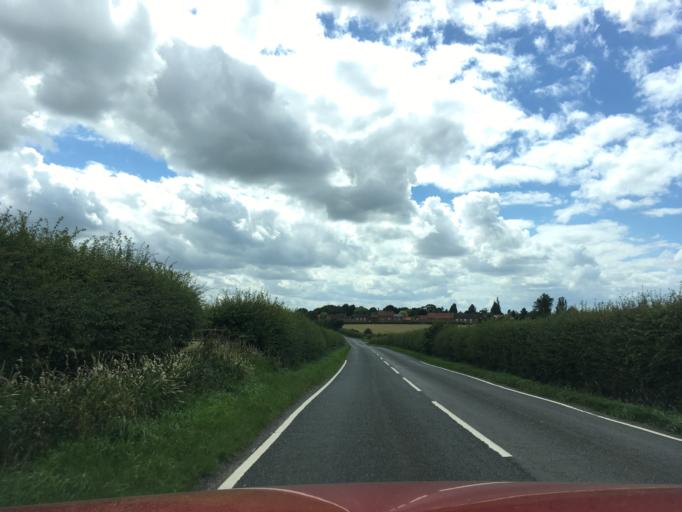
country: GB
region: England
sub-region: Nottinghamshire
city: Ruddington
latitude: 52.8761
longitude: -1.1246
